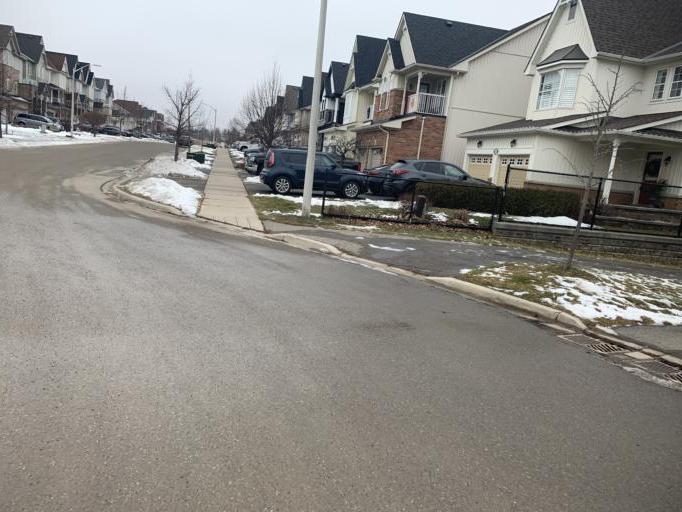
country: CA
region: Ontario
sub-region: Halton
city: Milton
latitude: 43.6595
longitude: -79.9220
